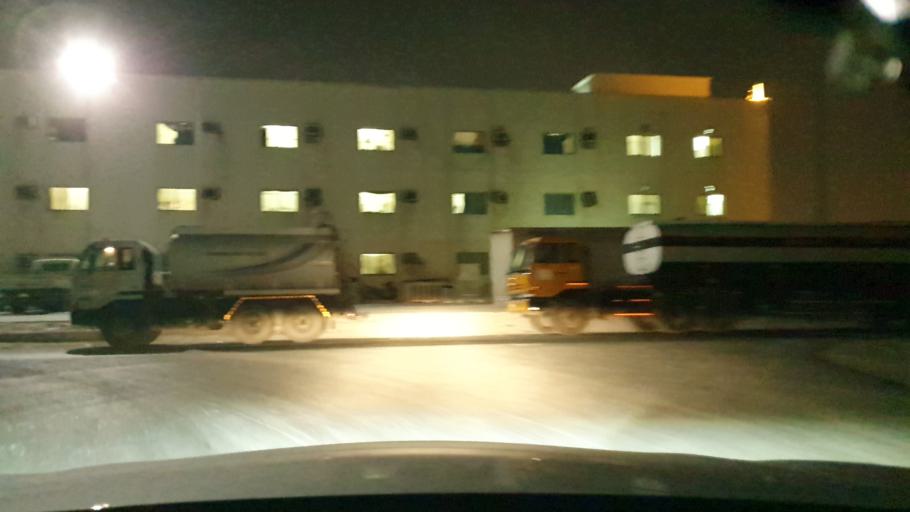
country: BH
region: Northern
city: Sitrah
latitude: 26.0973
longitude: 50.6149
